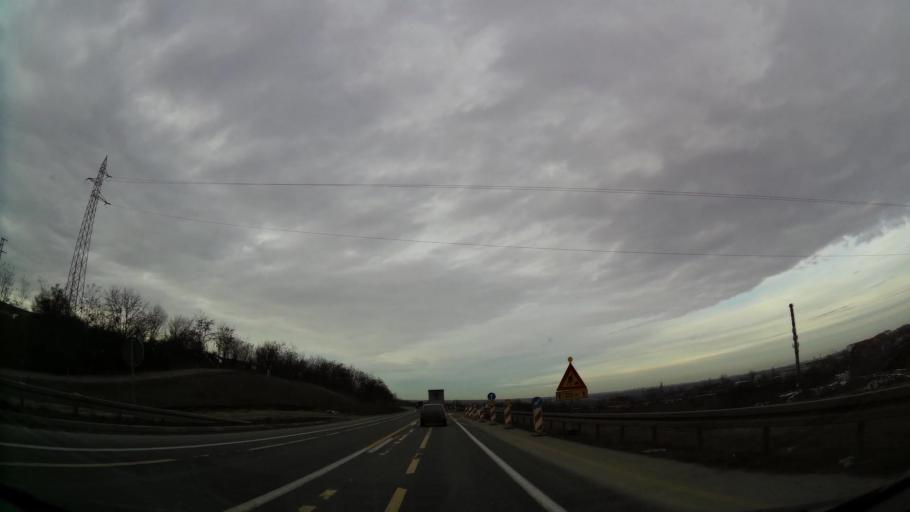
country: RS
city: Ostruznica
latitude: 44.7209
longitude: 20.3592
